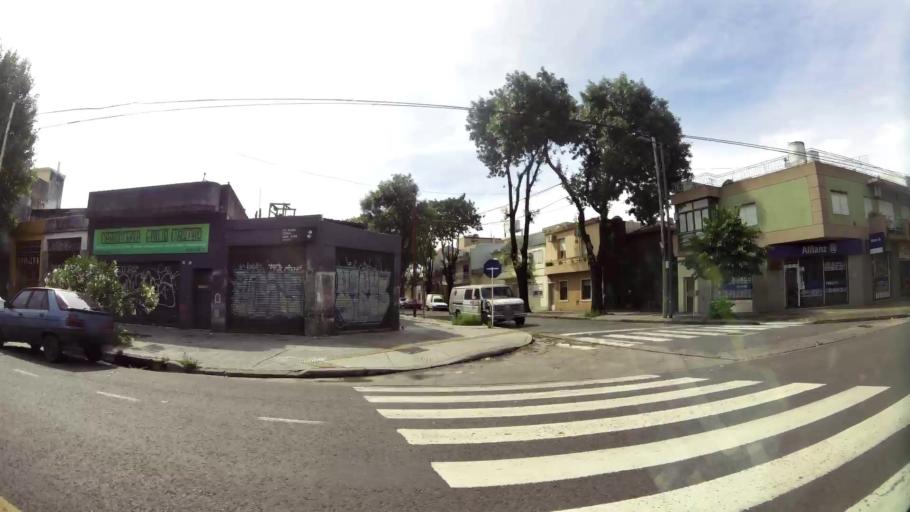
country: AR
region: Buenos Aires F.D.
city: Villa Santa Rita
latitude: -34.6484
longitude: -58.5077
